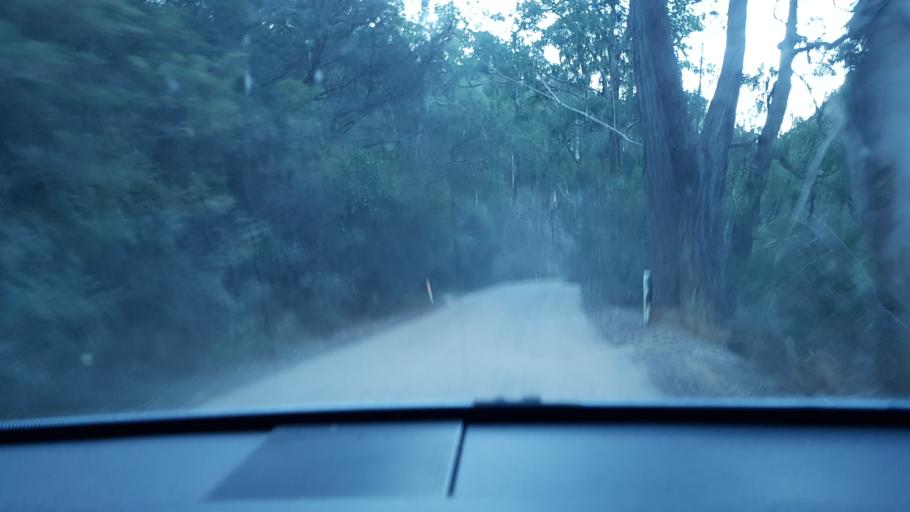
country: AU
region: New South Wales
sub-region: Lithgow
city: Portland
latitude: -33.1897
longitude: 150.2449
